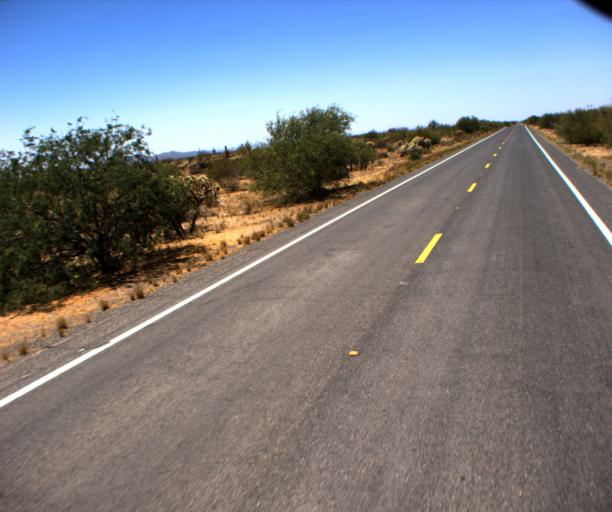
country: US
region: Arizona
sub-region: Pinal County
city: Florence
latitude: 32.7995
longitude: -111.1819
